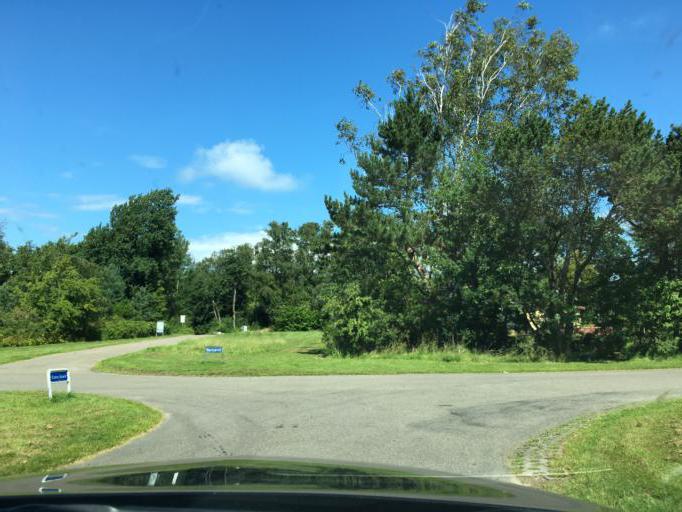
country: DK
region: Capital Region
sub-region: Gribskov Kommune
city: Helsinge
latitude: 56.0924
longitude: 12.1660
